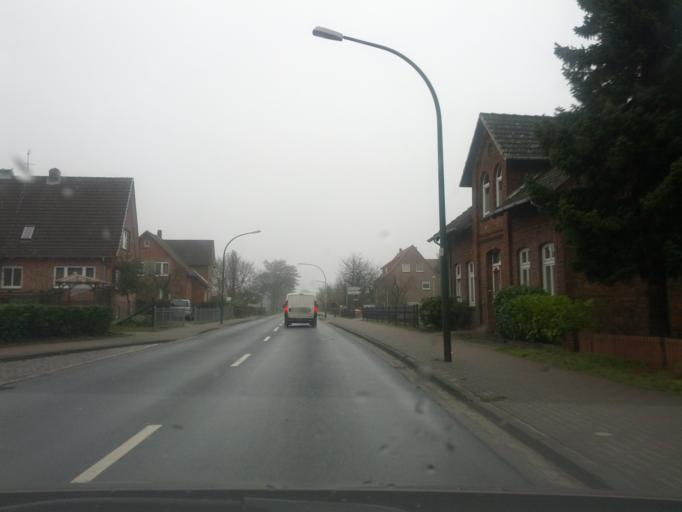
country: DE
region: Lower Saxony
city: Apensen
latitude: 53.4357
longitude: 9.6130
